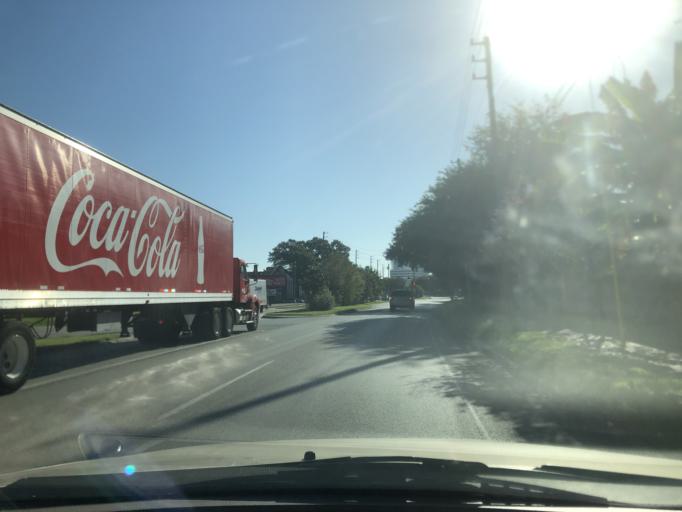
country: US
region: Texas
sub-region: Harris County
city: Bunker Hill Village
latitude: 29.7479
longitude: -95.5710
